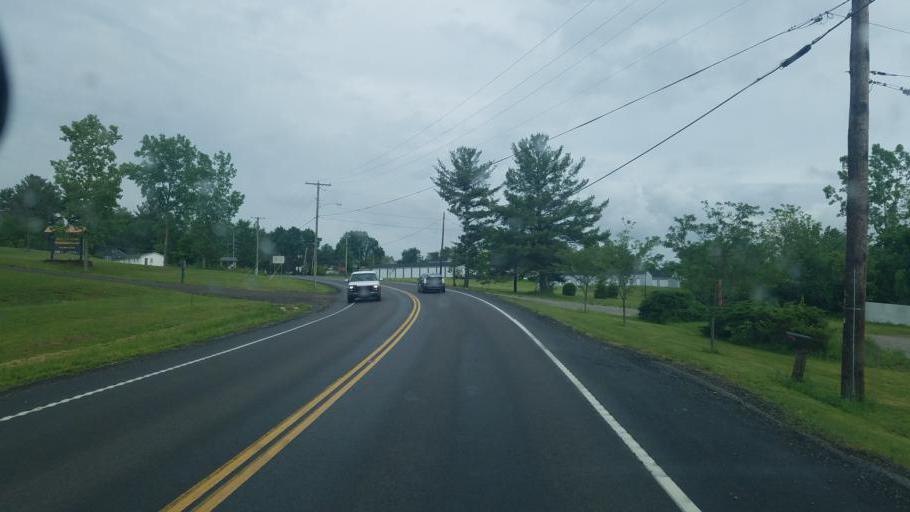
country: US
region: Ohio
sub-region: Knox County
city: Mount Vernon
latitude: 40.4117
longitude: -82.4976
